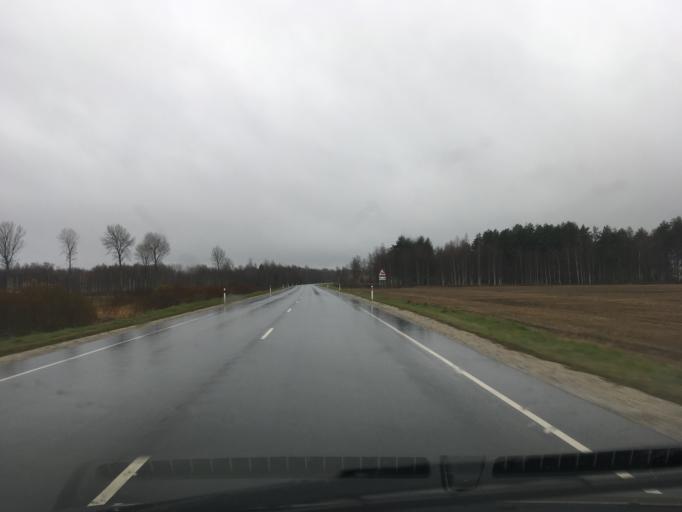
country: EE
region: Harju
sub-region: Nissi vald
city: Turba
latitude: 58.8544
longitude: 24.0703
